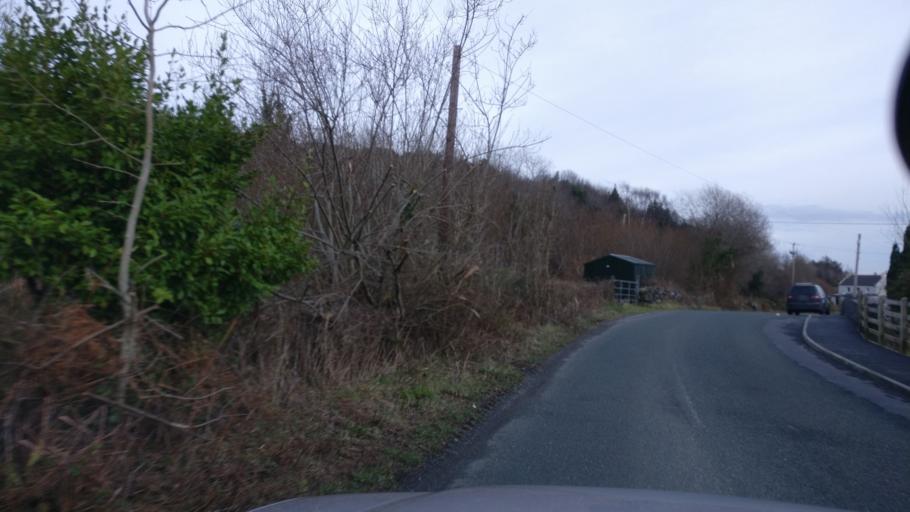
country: IE
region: Connaught
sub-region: County Galway
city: Oughterard
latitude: 53.5198
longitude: -9.4557
